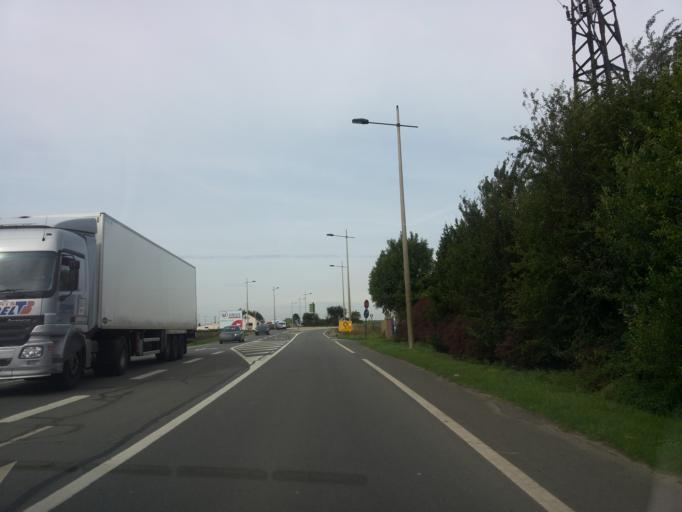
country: FR
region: Nord-Pas-de-Calais
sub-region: Departement du Pas-de-Calais
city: Marquion
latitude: 50.2154
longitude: 3.0697
